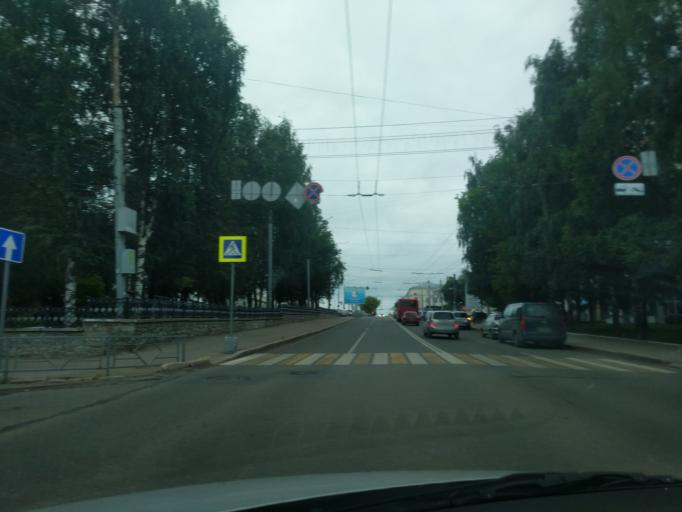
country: RU
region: Kirov
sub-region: Kirovo-Chepetskiy Rayon
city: Kirov
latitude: 58.5962
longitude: 49.6687
